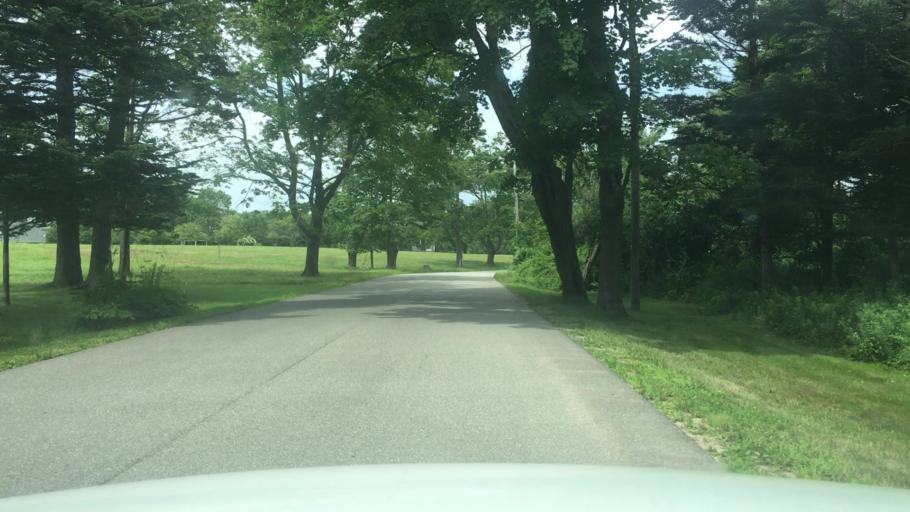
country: US
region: Maine
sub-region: Cumberland County
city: Scarborough
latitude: 43.5570
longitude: -70.2659
